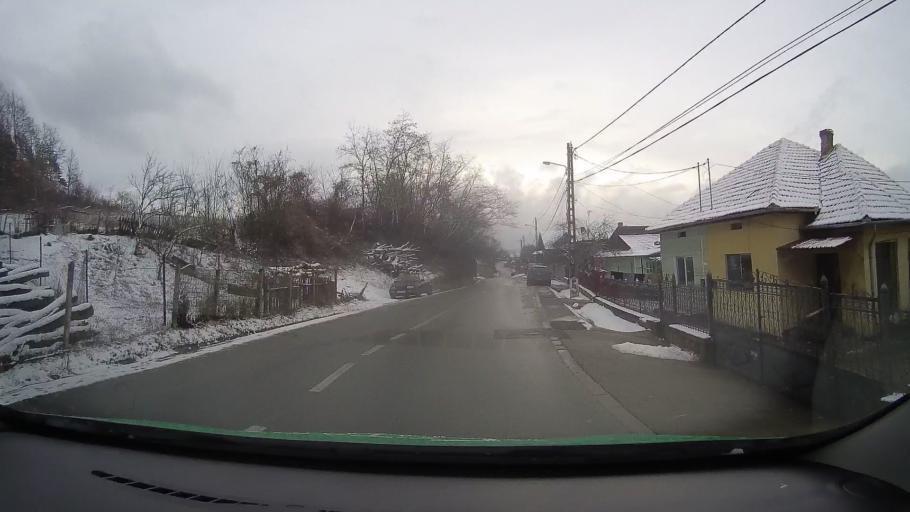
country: RO
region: Hunedoara
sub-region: Oras Hateg
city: Hateg
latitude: 45.6251
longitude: 22.9364
